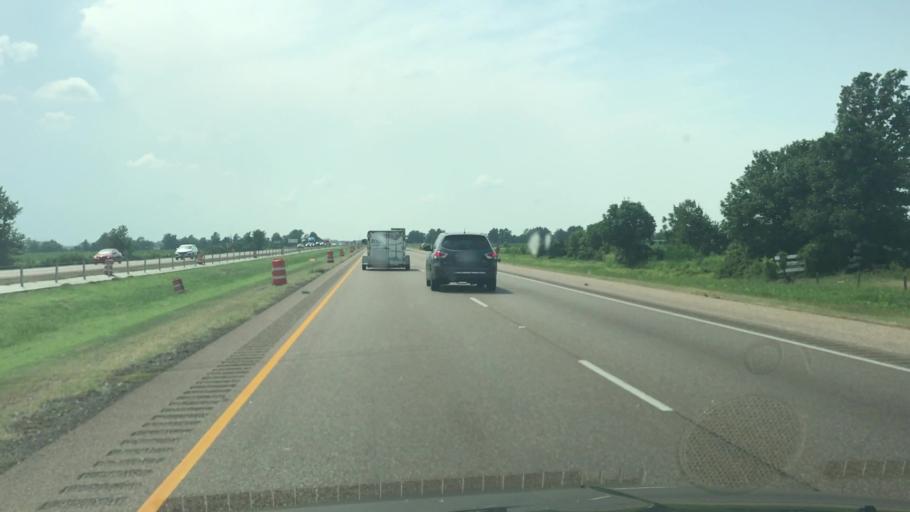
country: US
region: Arkansas
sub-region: Crittenden County
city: Earle
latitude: 35.1508
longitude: -90.3815
